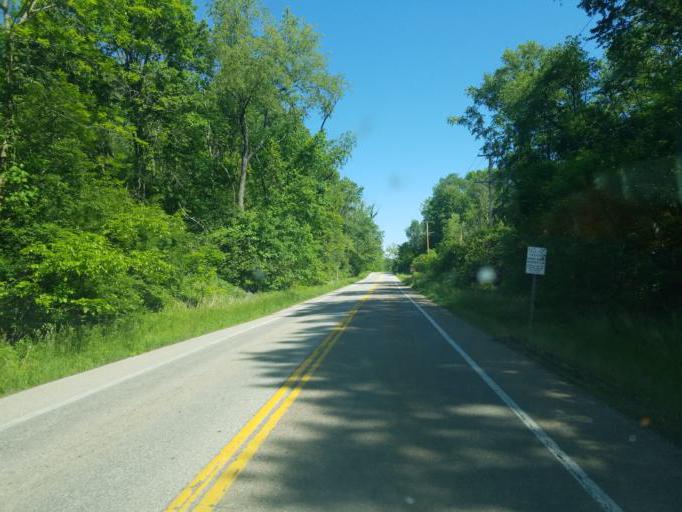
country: US
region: Ohio
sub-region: Summit County
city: Fairlawn
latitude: 41.1644
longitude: -81.5673
